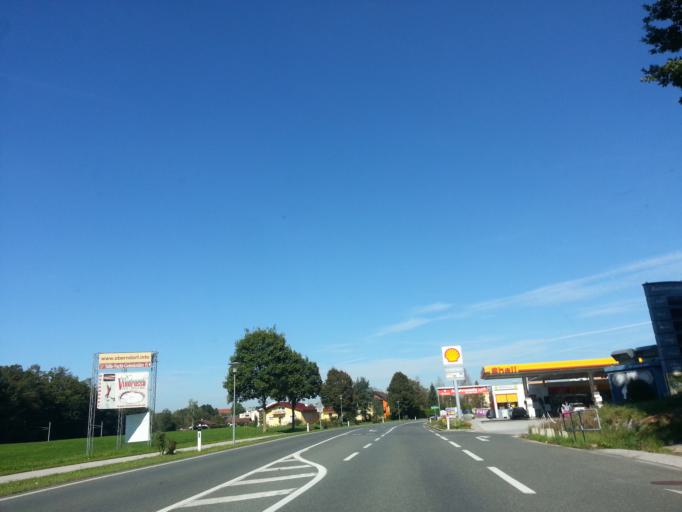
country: DE
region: Bavaria
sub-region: Upper Bavaria
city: Laufen
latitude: 47.9336
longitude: 12.9469
